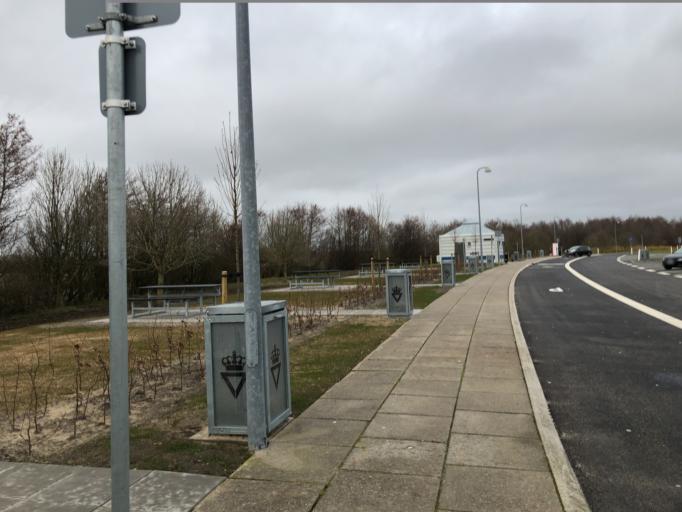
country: DK
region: North Denmark
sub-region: Bronderslev Kommune
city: Hjallerup
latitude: 57.1538
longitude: 10.1569
